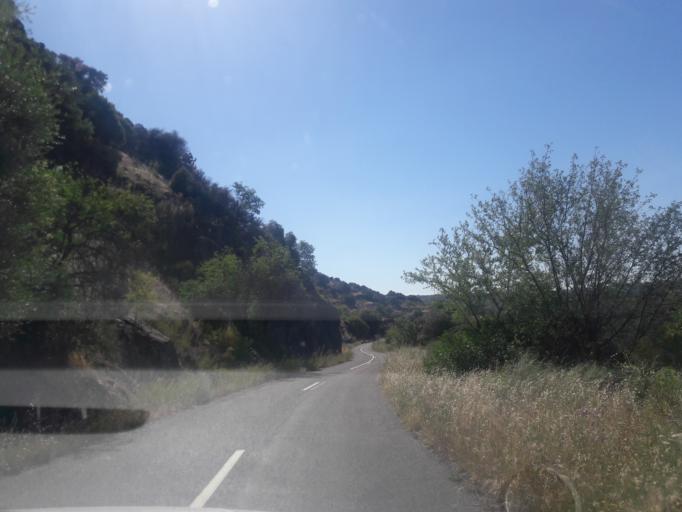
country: ES
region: Castille and Leon
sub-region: Provincia de Salamanca
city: Saucelle
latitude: 41.0322
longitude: -6.7595
